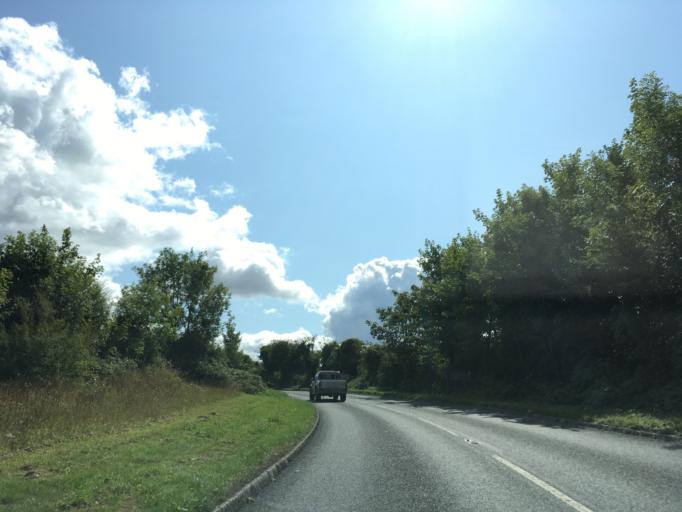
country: GB
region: England
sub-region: Hampshire
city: Winchester
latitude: 51.0471
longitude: -1.3022
